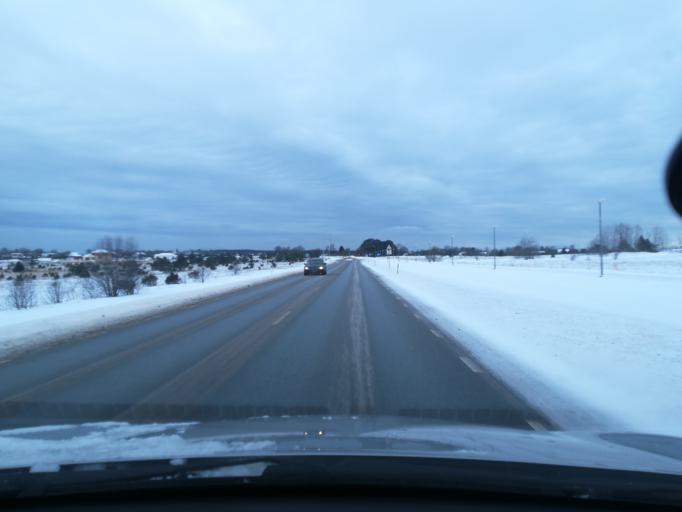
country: EE
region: Harju
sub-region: Harku vald
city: Tabasalu
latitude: 59.4509
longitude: 24.4590
